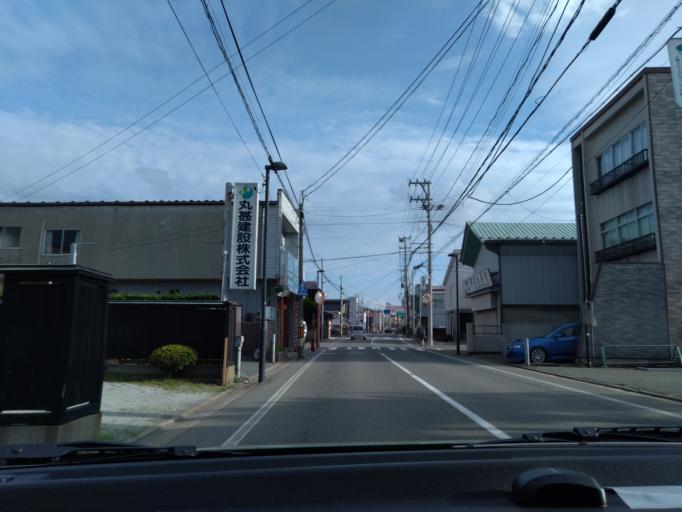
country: JP
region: Akita
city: Akita Shi
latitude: 39.7590
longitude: 140.0694
